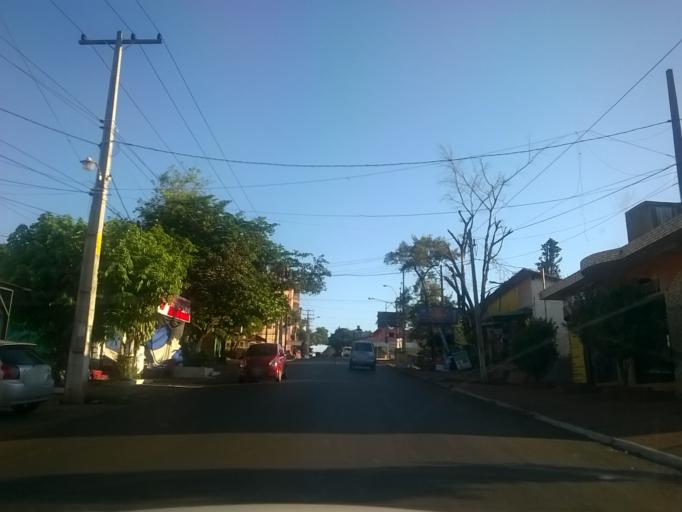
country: PY
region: Alto Parana
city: Presidente Franco
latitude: -25.5488
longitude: -54.6084
